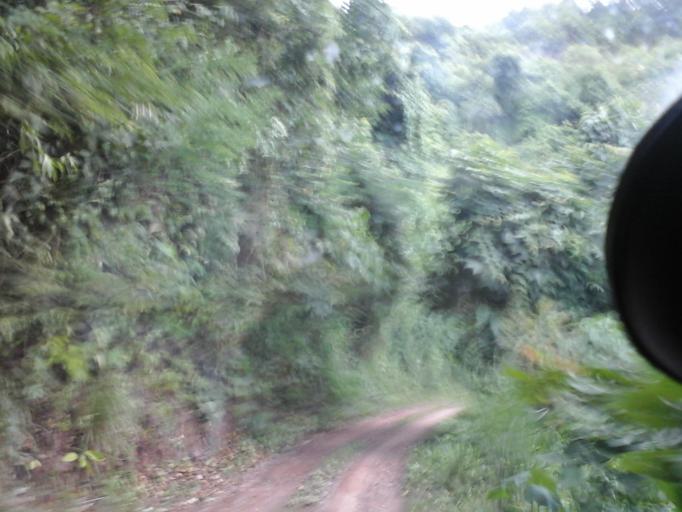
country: CO
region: Cesar
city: San Diego
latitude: 10.2700
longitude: -73.0813
